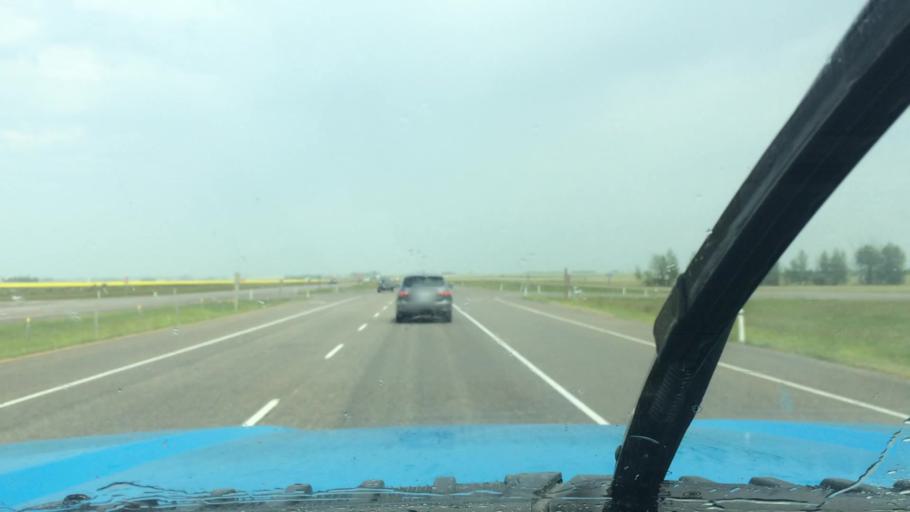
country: CA
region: Alberta
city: Carstairs
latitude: 51.6194
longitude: -114.0253
